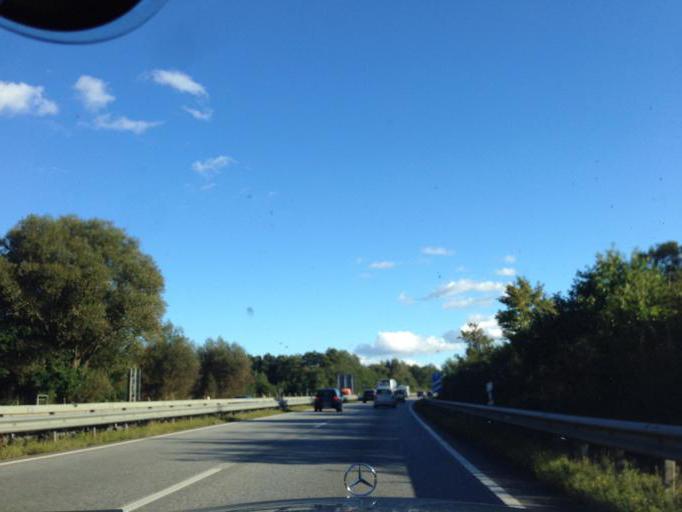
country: DE
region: Schleswig-Holstein
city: Schackendorf
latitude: 53.9641
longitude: 10.2569
